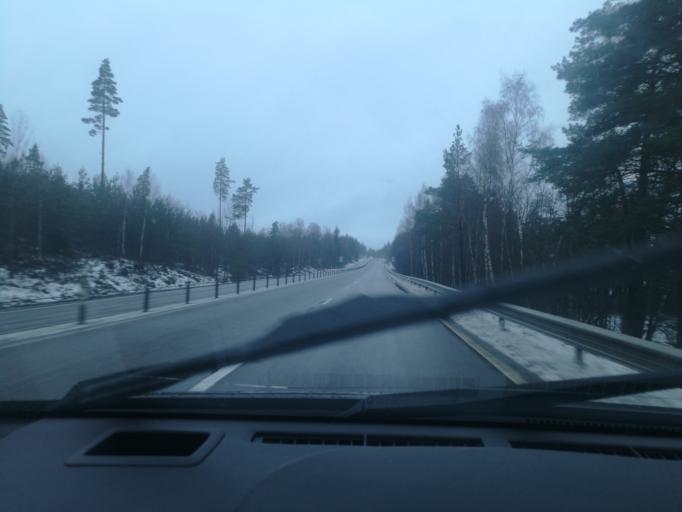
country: SE
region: OEstergoetland
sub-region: Norrkopings Kommun
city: Jursla
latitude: 58.7556
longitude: 16.1751
